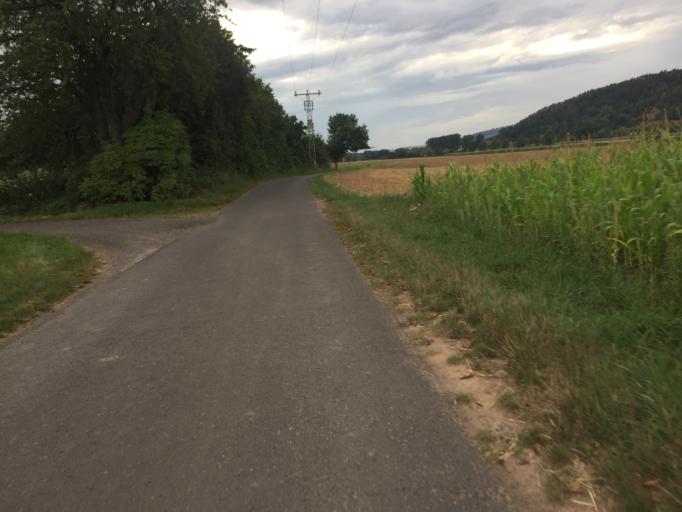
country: DE
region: Hesse
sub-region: Regierungsbezirk Kassel
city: Alheim
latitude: 51.0480
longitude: 9.6540
